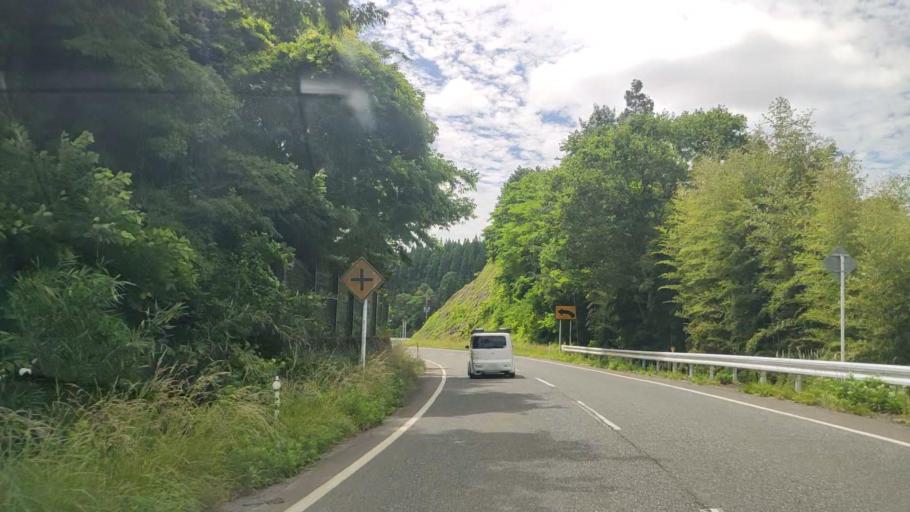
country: JP
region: Okayama
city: Niimi
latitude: 35.1736
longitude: 133.5719
